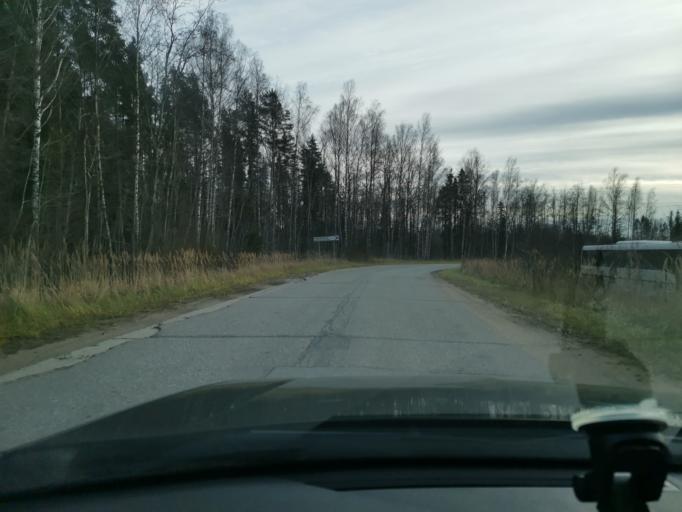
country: EE
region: Ida-Virumaa
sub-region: Sillamaee linn
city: Sillamae
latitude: 59.2710
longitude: 27.9136
